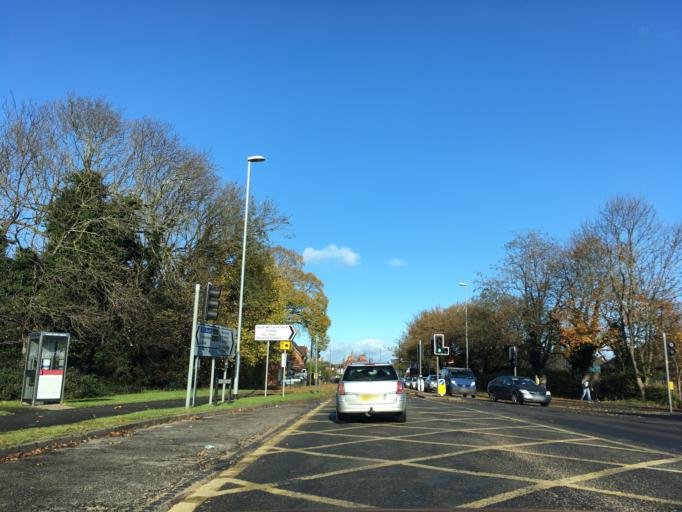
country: GB
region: England
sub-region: Worcestershire
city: Evesham
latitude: 52.0814
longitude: -1.9513
